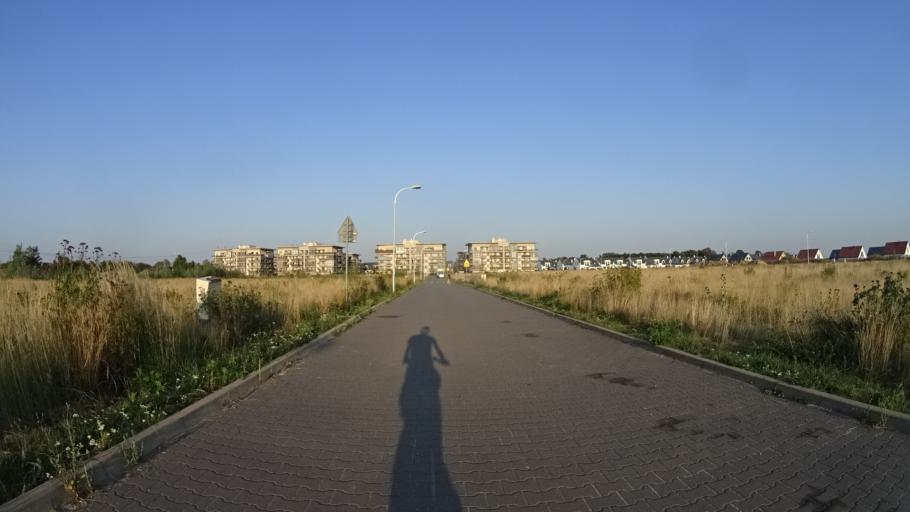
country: PL
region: Masovian Voivodeship
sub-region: Powiat warszawski zachodni
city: Ozarow Mazowiecki
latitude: 52.2359
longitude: 20.7749
